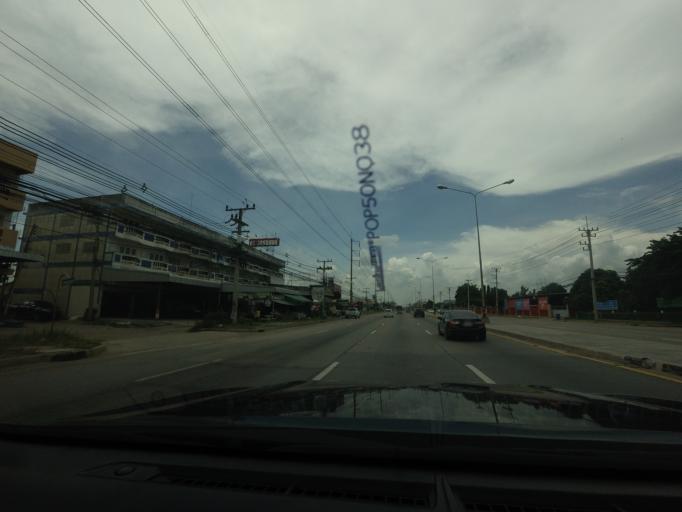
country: TH
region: Nakhon Pathom
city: Nakhon Pathom
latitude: 13.8480
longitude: 100.0216
